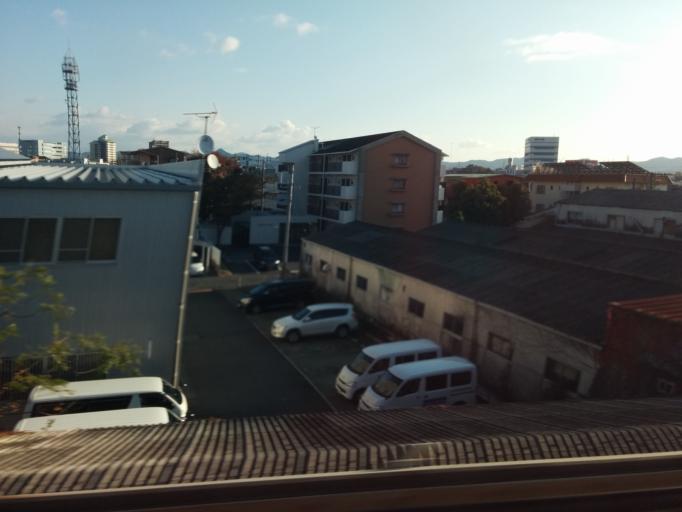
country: JP
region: Aichi
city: Toyohashi
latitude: 34.7548
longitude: 137.3854
